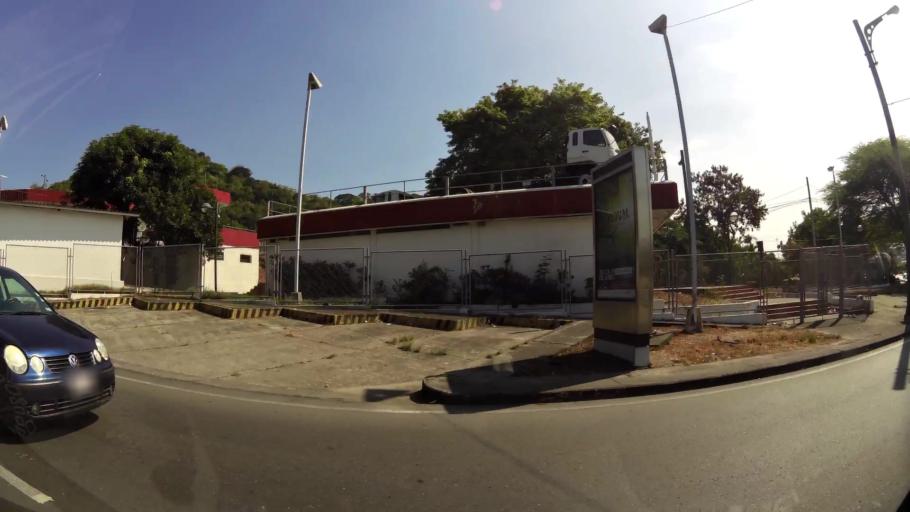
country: EC
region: Guayas
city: Guayaquil
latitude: -2.1630
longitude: -79.9244
